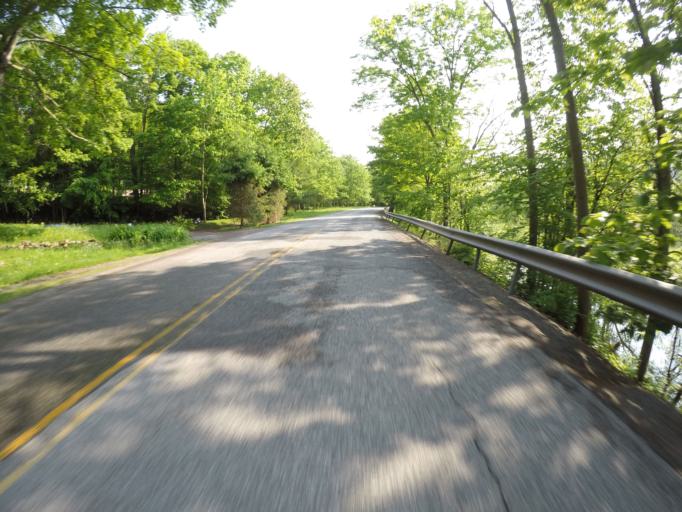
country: US
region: New York
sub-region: Delaware County
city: Stamford
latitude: 42.1346
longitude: -74.6668
